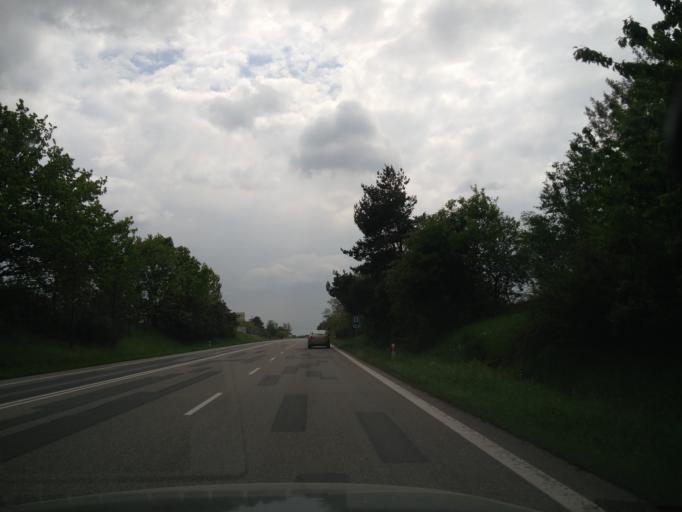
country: CZ
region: Jihocesky
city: Kamenny Ujezd
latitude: 48.9019
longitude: 14.4404
